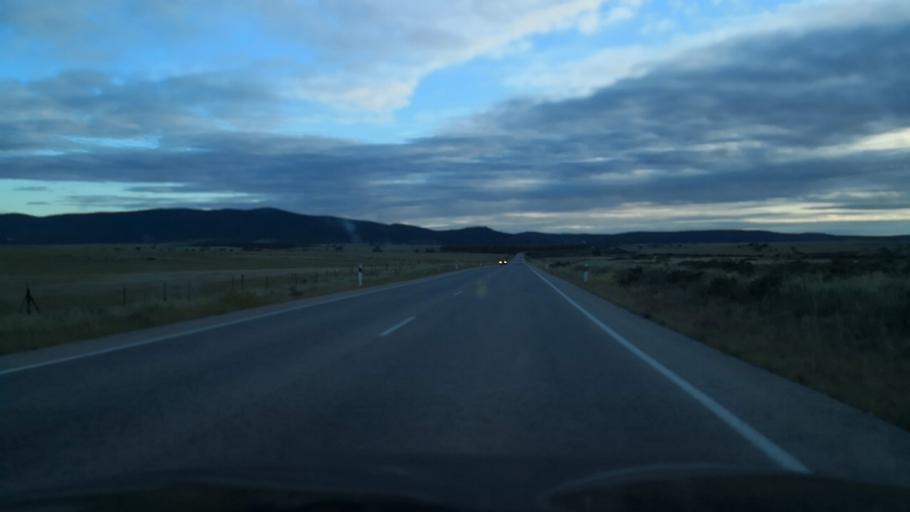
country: ES
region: Extremadura
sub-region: Provincia de Caceres
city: Malpartida de Caceres
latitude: 39.3443
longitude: -6.4742
